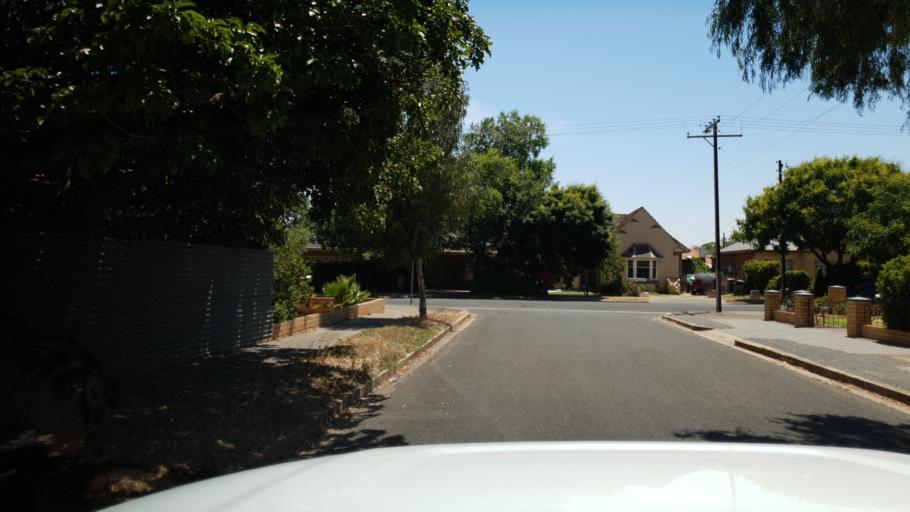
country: AU
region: South Australia
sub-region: Mitcham
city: Clarence Gardens
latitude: -34.9767
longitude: 138.5859
